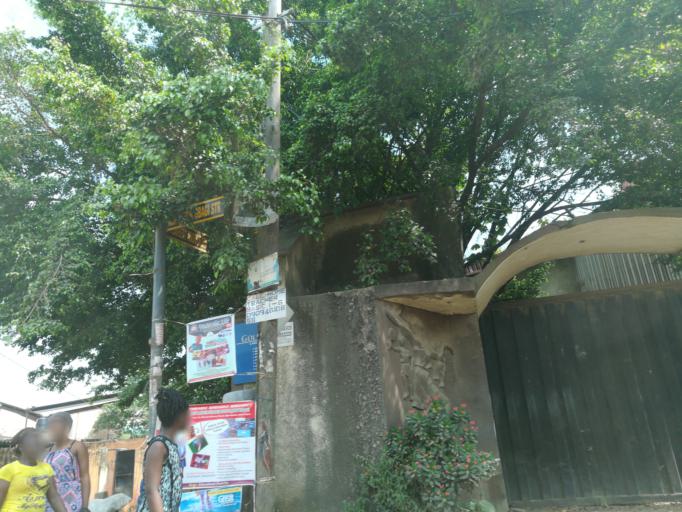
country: NG
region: Lagos
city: Oshodi
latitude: 6.5455
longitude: 3.3247
